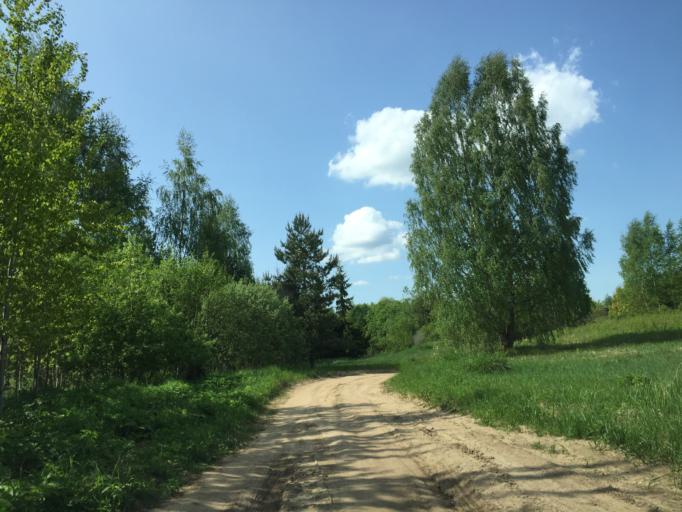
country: LV
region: Baldone
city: Baldone
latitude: 56.7886
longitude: 24.4160
